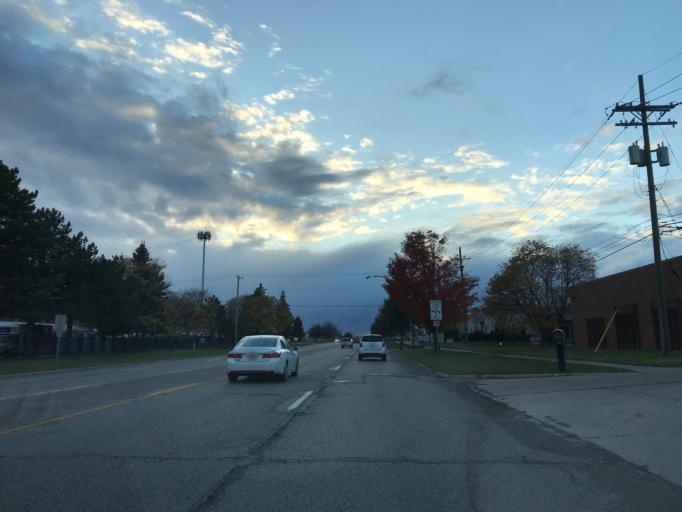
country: US
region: Michigan
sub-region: Oakland County
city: Farmington
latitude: 42.4409
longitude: -83.3676
